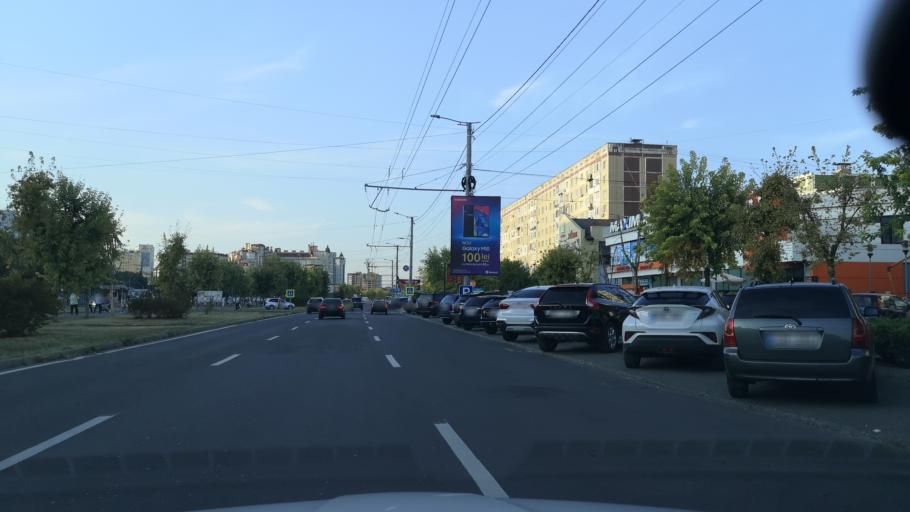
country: MD
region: Chisinau
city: Stauceni
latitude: 47.0491
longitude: 28.8907
